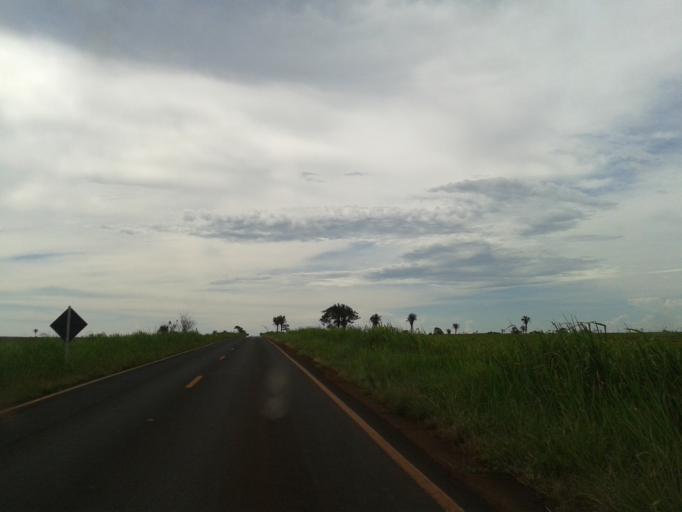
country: BR
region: Minas Gerais
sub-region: Capinopolis
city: Capinopolis
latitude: -18.6913
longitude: -49.3871
